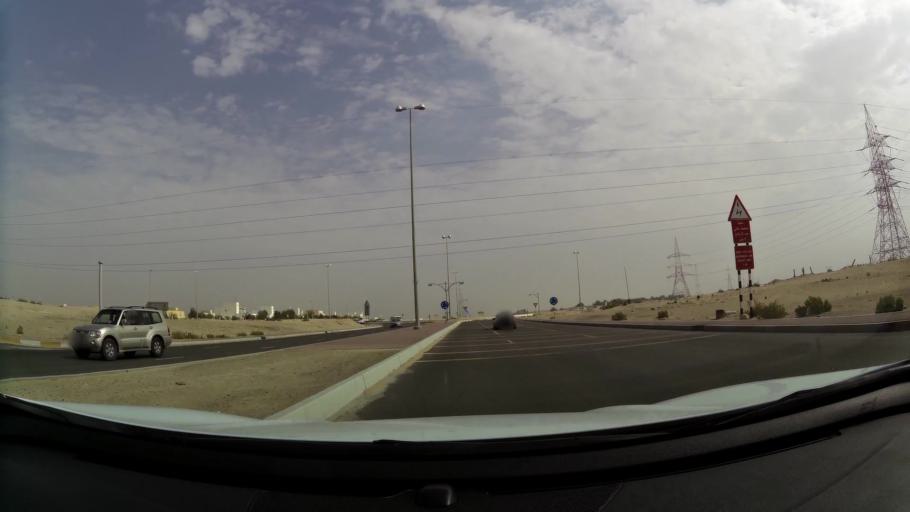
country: AE
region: Abu Dhabi
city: Abu Dhabi
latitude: 24.2950
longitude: 54.6609
